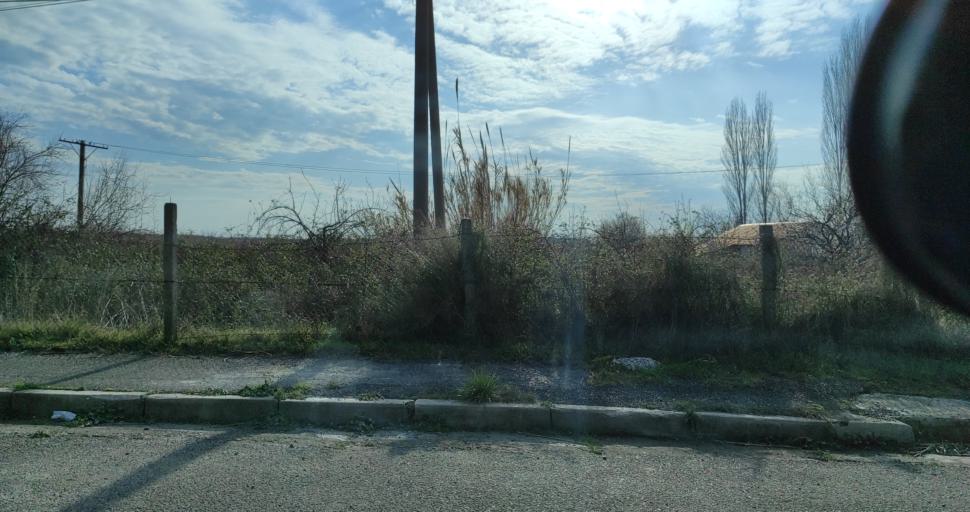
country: AL
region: Lezhe
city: Lezhe
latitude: 41.7933
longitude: 19.6220
